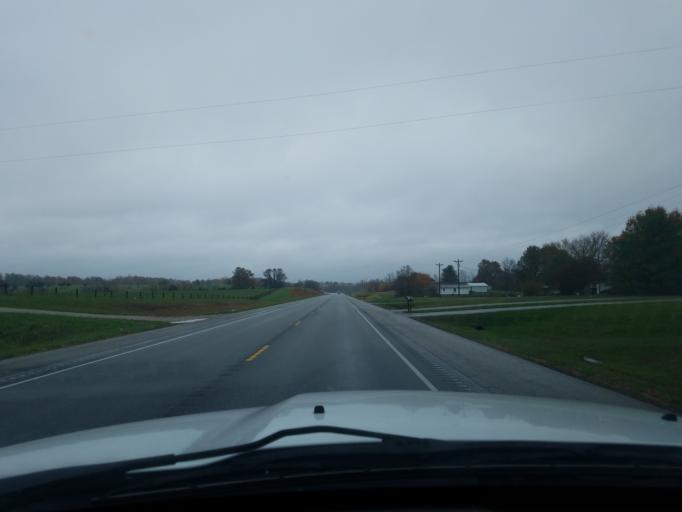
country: US
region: Kentucky
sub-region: Larue County
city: Hodgenville
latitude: 37.5295
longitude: -85.6832
